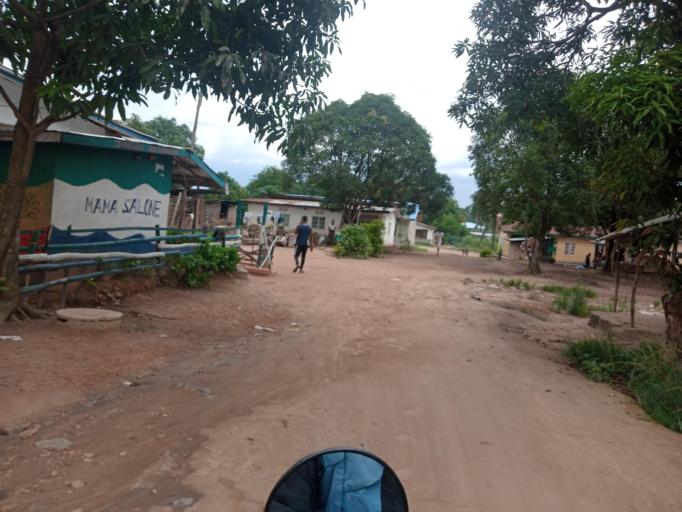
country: SL
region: Southern Province
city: Bo
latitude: 7.9819
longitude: -11.7430
